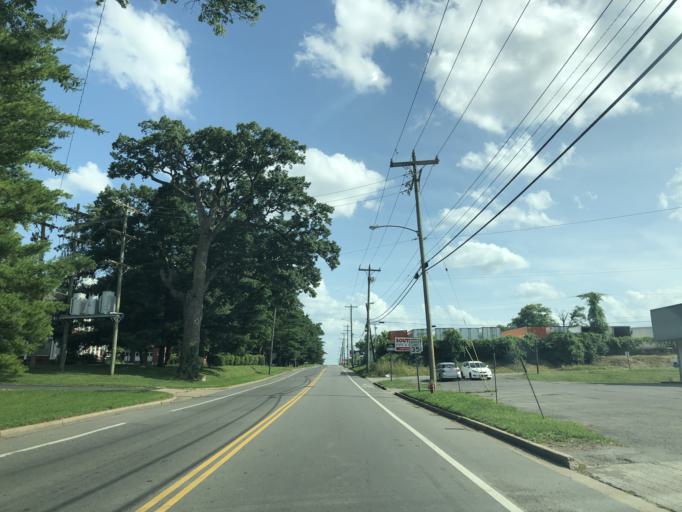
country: US
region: Tennessee
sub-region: Davidson County
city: Nashville
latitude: 36.1339
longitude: -86.7414
